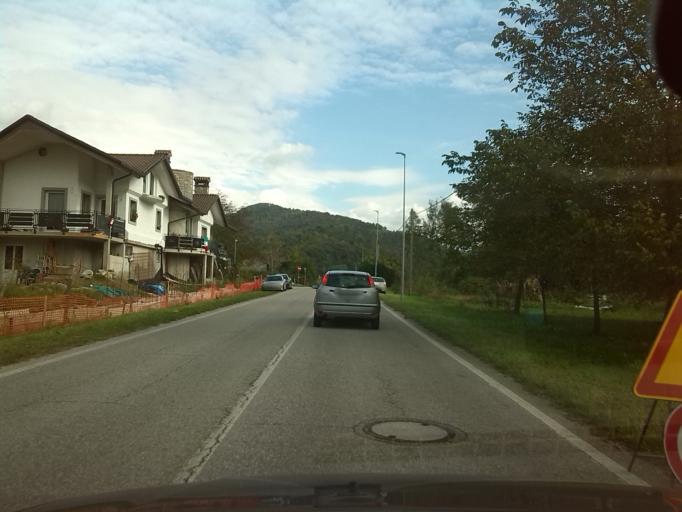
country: IT
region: Friuli Venezia Giulia
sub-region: Provincia di Udine
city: Merso di Sopra
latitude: 46.1185
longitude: 13.5168
